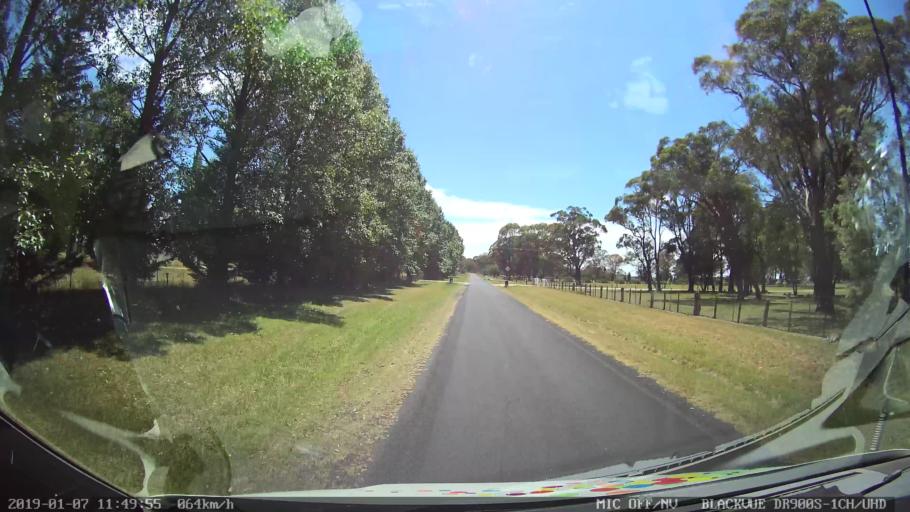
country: AU
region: New South Wales
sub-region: Guyra
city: Guyra
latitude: -30.3148
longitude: 151.6309
